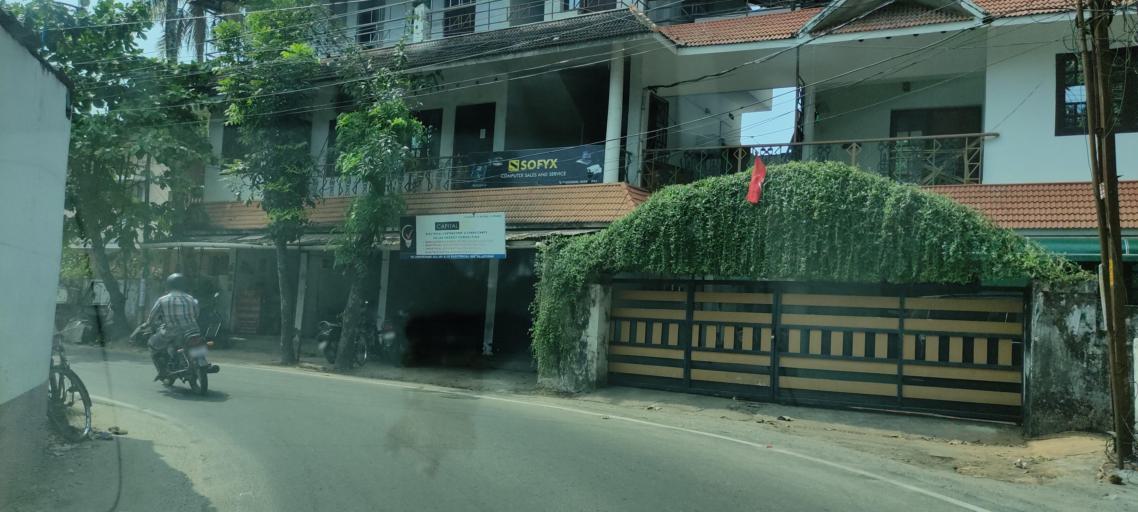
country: IN
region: Kerala
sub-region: Alappuzha
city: Alleppey
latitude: 9.5076
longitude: 76.3341
